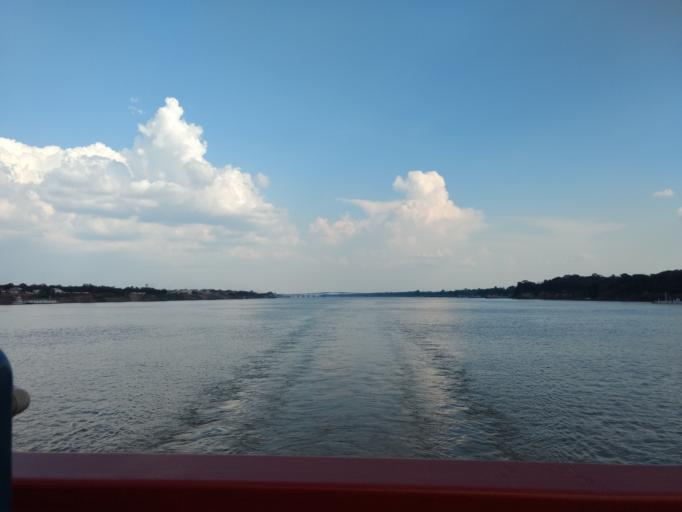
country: BR
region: Rondonia
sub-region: Porto Velho
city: Porto Velho
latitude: -8.6954
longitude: -63.9222
